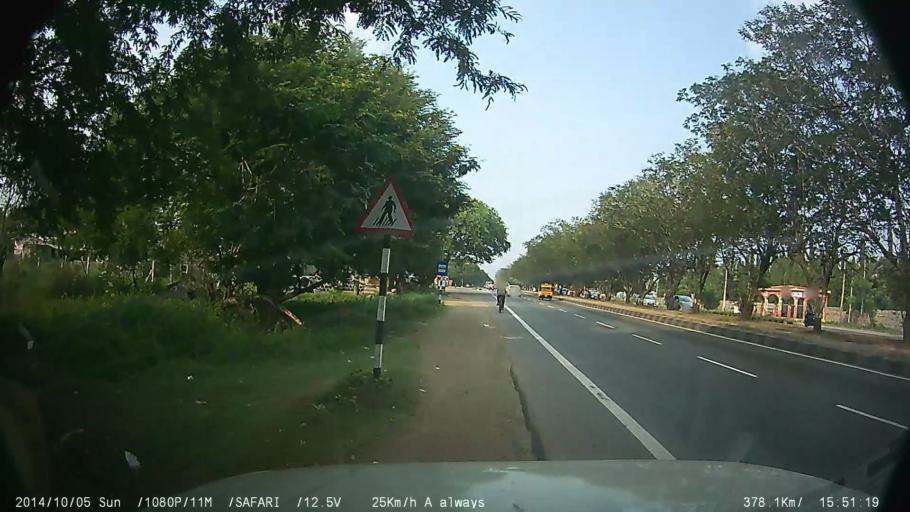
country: IN
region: Tamil Nadu
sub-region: Kancheepuram
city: Singapperumalkovil
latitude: 12.7892
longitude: 80.0163
